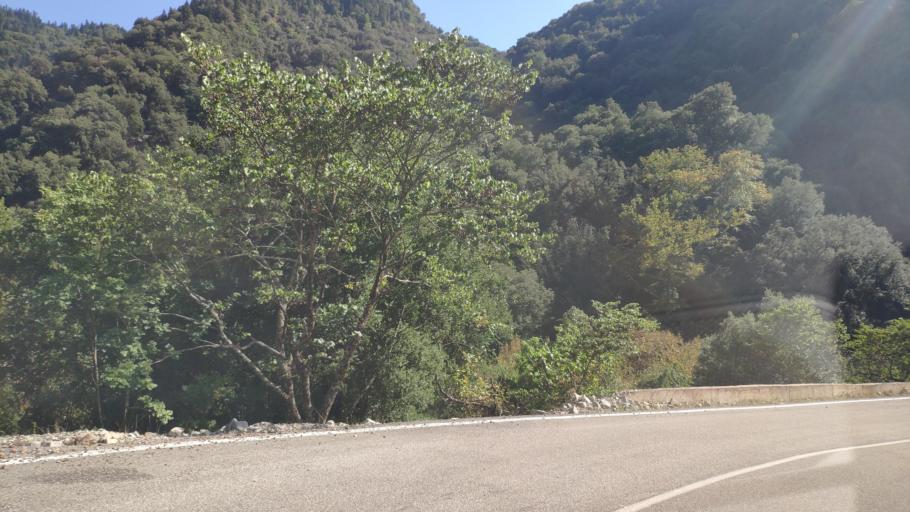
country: GR
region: Central Greece
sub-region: Nomos Evrytanias
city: Kerasochori
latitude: 39.0901
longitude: 21.6049
